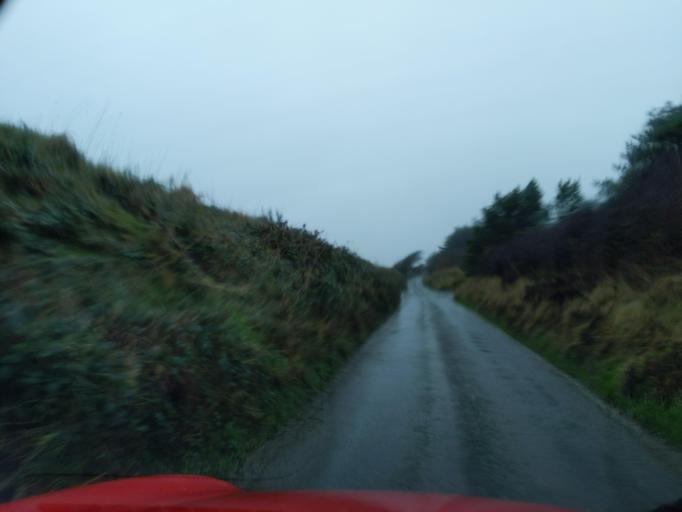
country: GB
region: England
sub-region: Cornwall
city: Camelford
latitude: 50.6479
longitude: -4.6995
